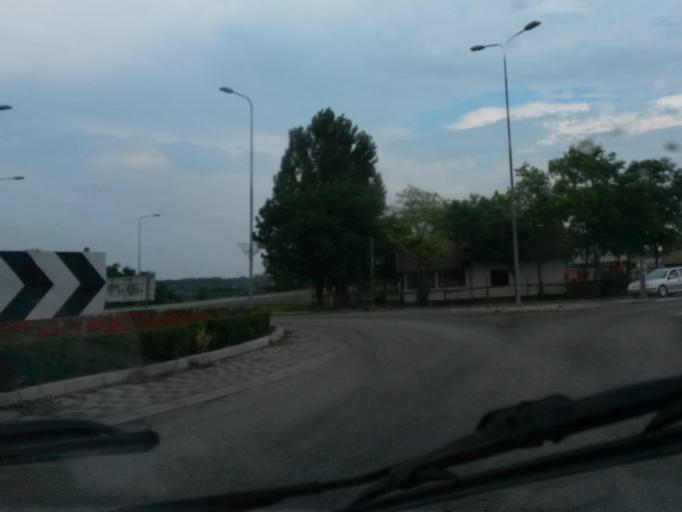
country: RS
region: Autonomna Pokrajina Vojvodina
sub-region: Zapadnobacki Okrug
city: Apatin
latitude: 45.6702
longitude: 19.0306
